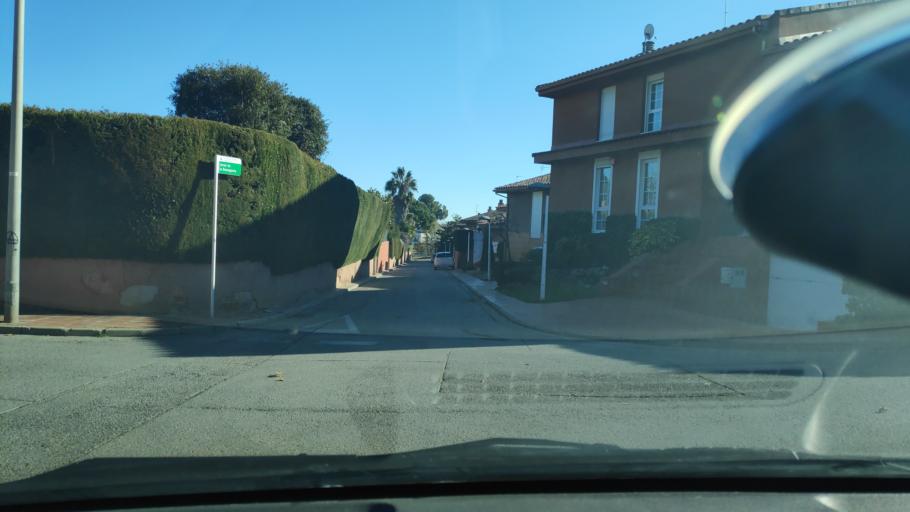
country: ES
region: Catalonia
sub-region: Provincia de Barcelona
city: Sant Quirze del Valles
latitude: 41.5263
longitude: 2.0733
